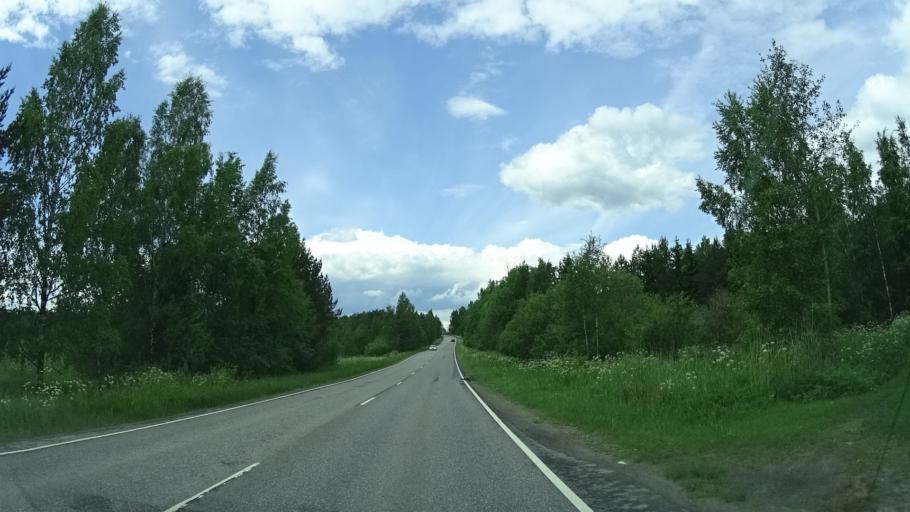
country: FI
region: Uusimaa
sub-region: Helsinki
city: Espoo
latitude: 60.1954
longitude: 24.5612
